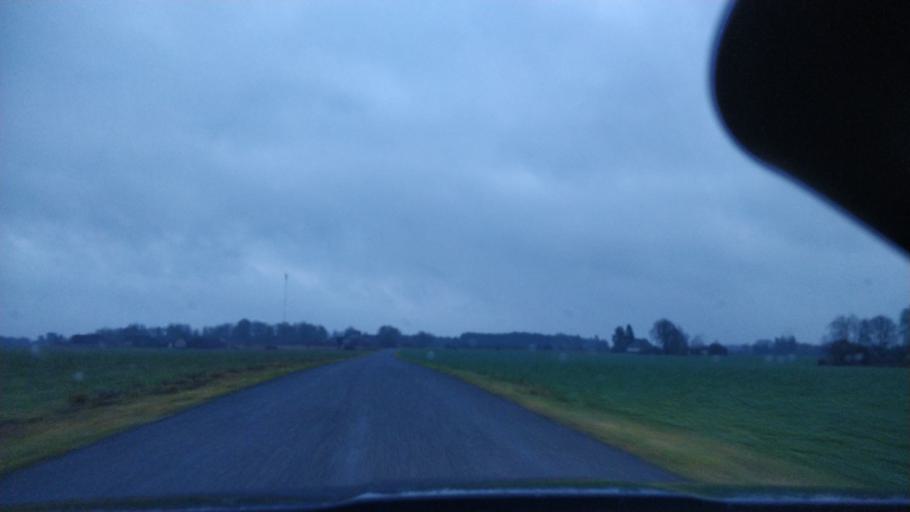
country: EE
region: Laeaene
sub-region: Lihula vald
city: Lihula
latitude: 58.8446
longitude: 24.0307
